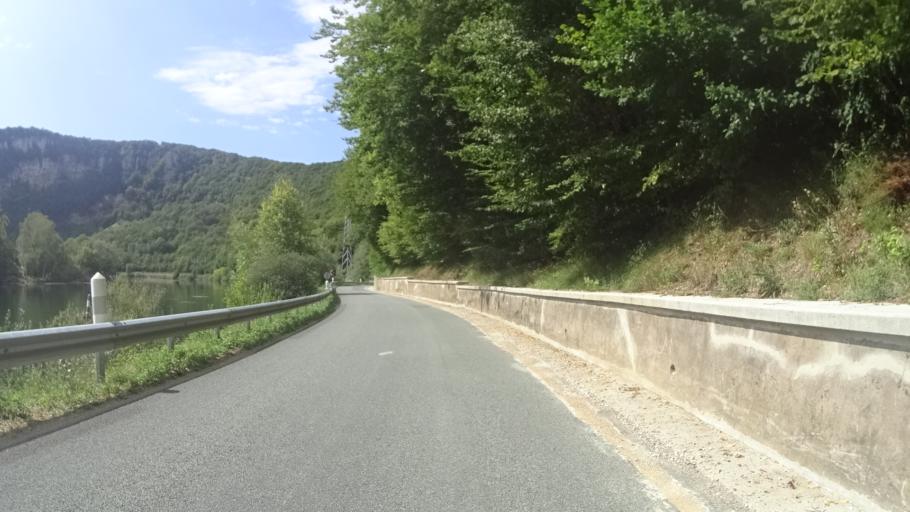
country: FR
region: Franche-Comte
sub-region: Departement du Doubs
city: Roulans
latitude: 47.3024
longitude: 6.2158
